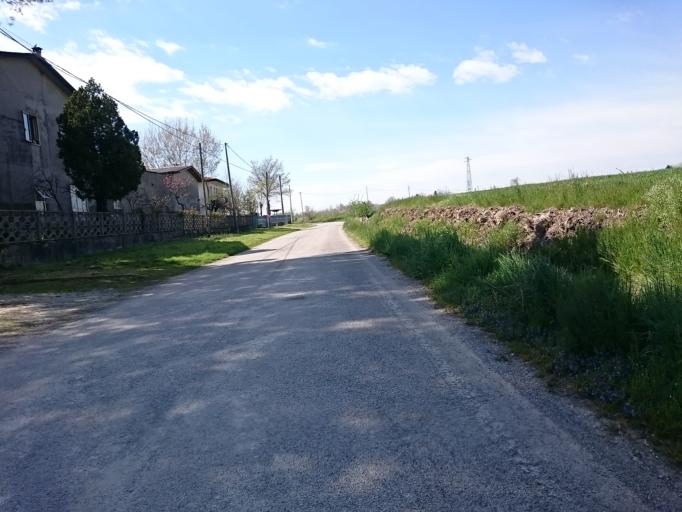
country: IT
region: Veneto
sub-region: Provincia di Padova
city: Brugine
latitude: 45.3075
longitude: 11.9803
